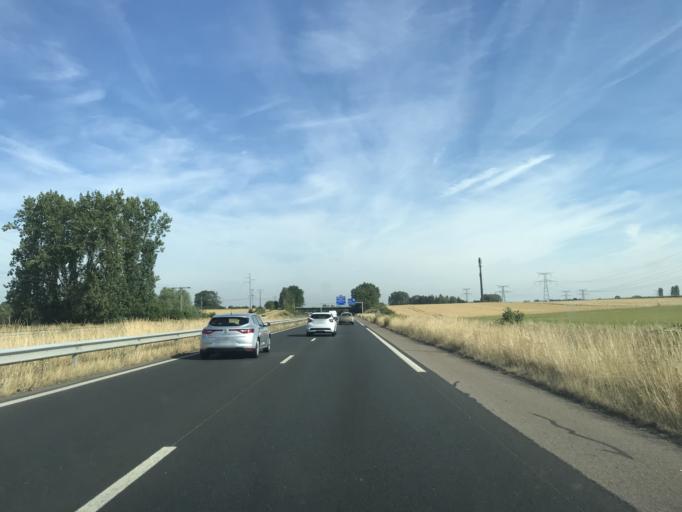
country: FR
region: Haute-Normandie
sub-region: Departement de la Seine-Maritime
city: La Vaupaliere
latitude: 49.5011
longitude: 0.9938
